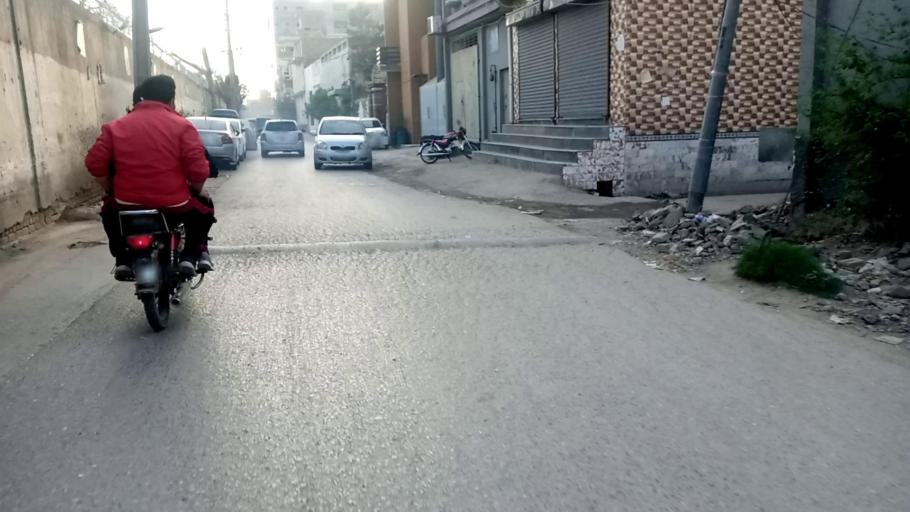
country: PK
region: Khyber Pakhtunkhwa
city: Peshawar
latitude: 34.0220
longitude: 71.5750
